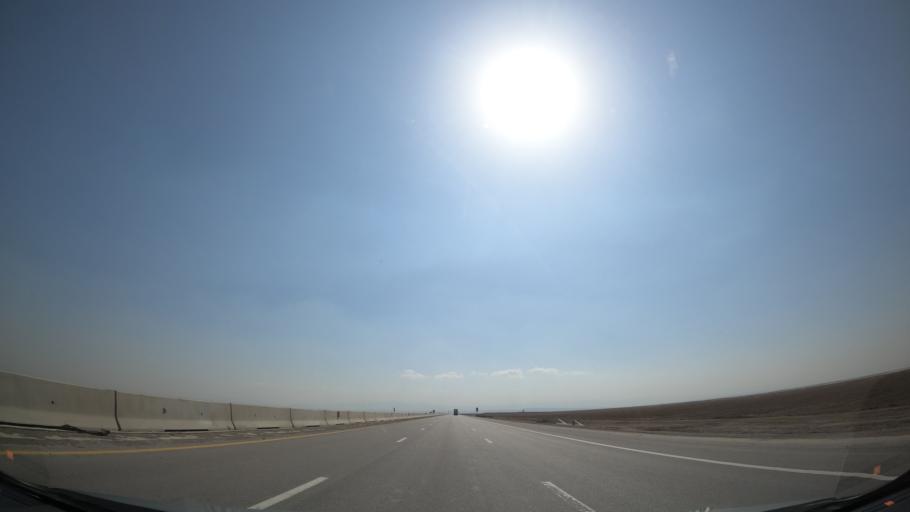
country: IR
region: Qazvin
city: Abyek
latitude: 35.9452
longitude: 50.4676
